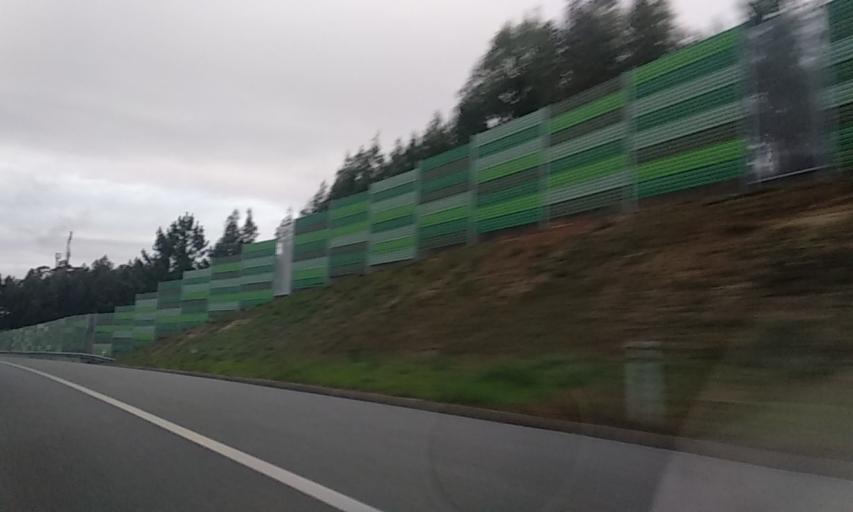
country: PT
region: Coimbra
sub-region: Condeixa-A-Nova
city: Condeixa-a-Nova
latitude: 40.1689
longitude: -8.4933
